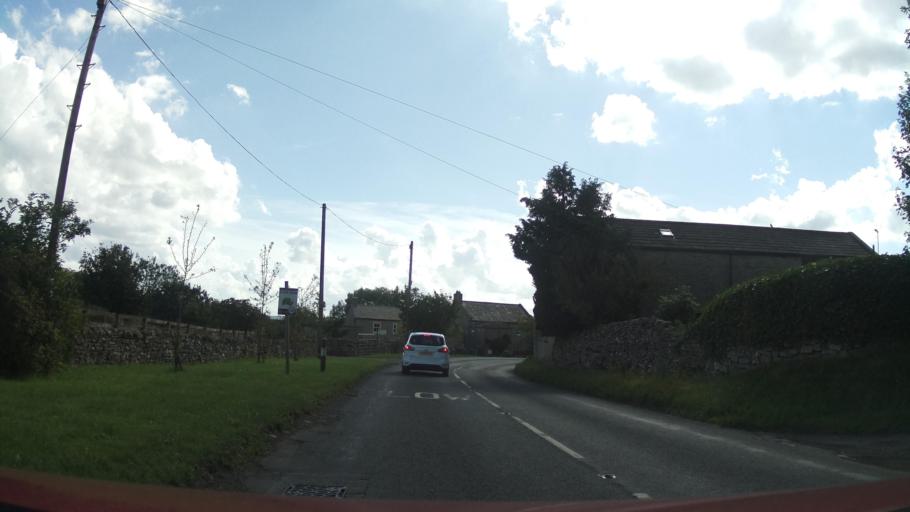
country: GB
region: England
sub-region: North Yorkshire
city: Leyburn
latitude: 54.3330
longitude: -1.8212
